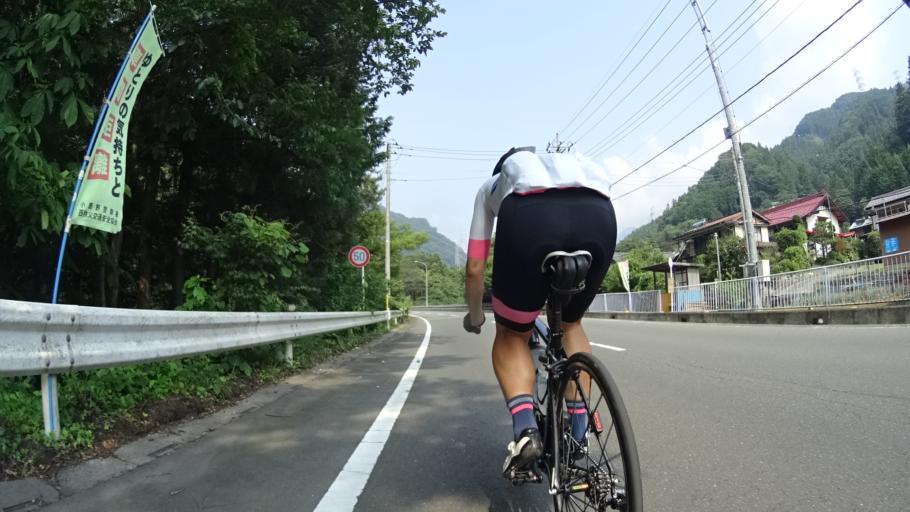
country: JP
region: Saitama
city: Chichibu
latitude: 36.0279
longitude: 138.9449
